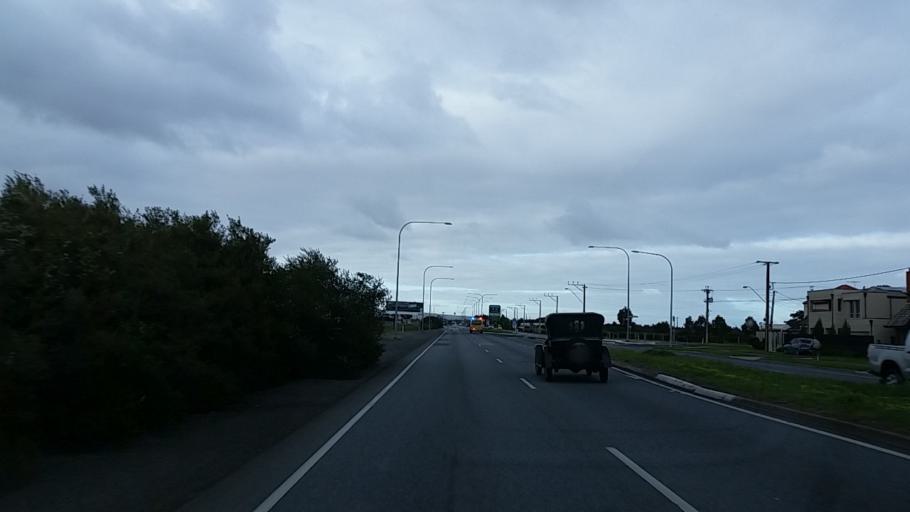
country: AU
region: South Australia
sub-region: Charles Sturt
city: Henley Beach
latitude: -34.9408
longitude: 138.5175
